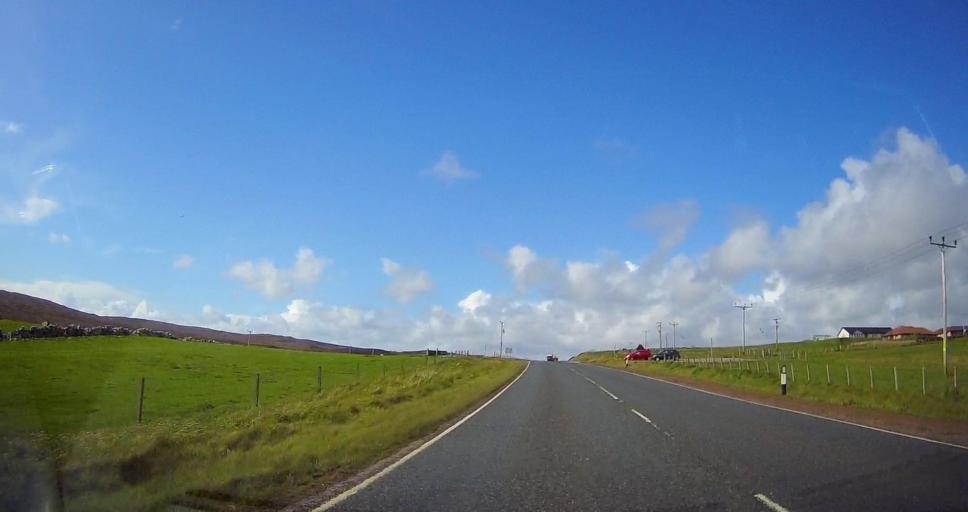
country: GB
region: Scotland
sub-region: Shetland Islands
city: Lerwick
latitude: 60.1974
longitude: -1.2320
